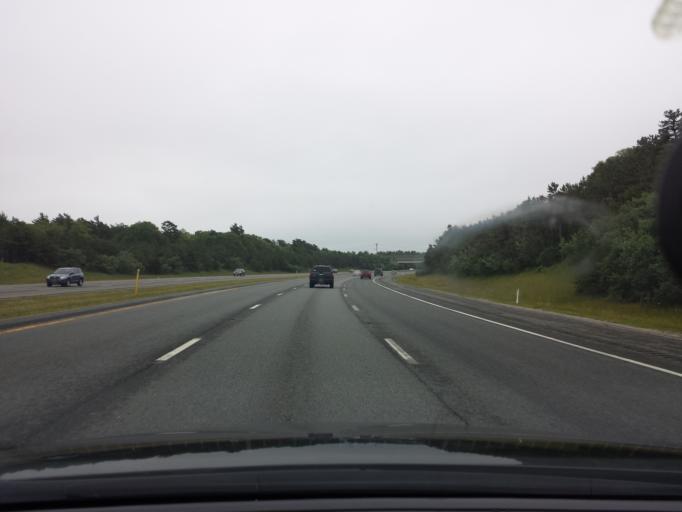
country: US
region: Massachusetts
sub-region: Barnstable County
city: Bourne
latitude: 41.7777
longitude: -70.5890
